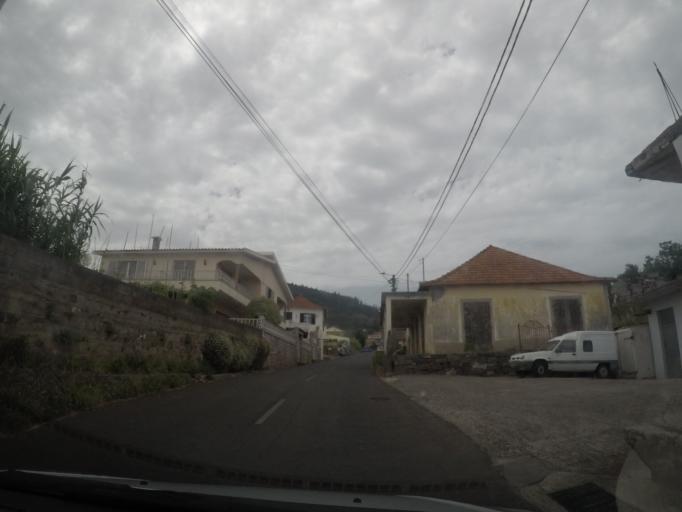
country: PT
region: Madeira
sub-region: Santa Cruz
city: Camacha
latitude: 32.6790
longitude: -16.8261
